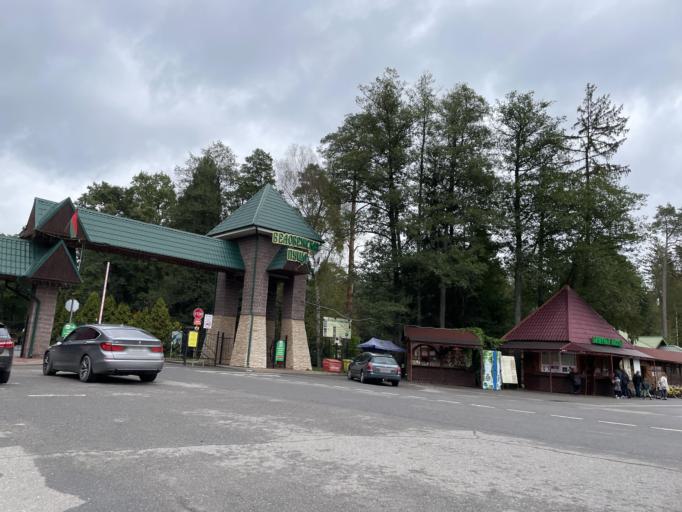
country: BY
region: Brest
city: Kamyanyuki
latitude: 52.5692
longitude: 23.8027
